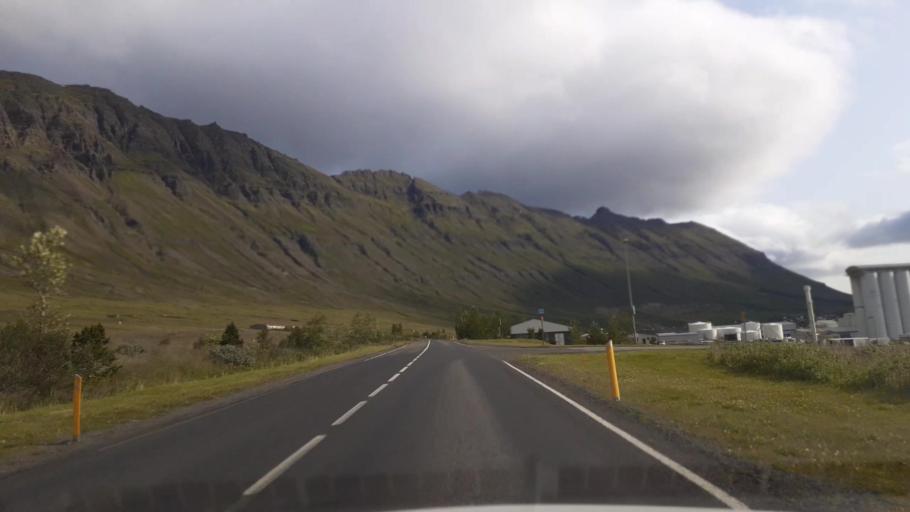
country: IS
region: East
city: Neskaupstadur
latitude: 65.1376
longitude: -13.7464
